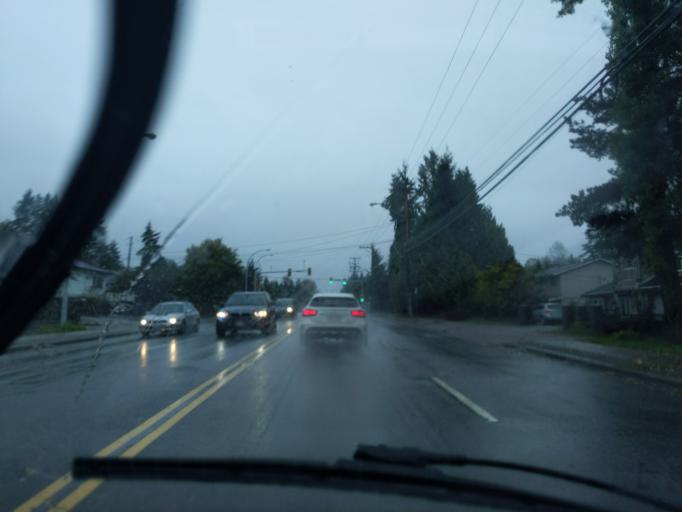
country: CA
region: British Columbia
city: New Westminster
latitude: 49.1988
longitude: -122.8299
